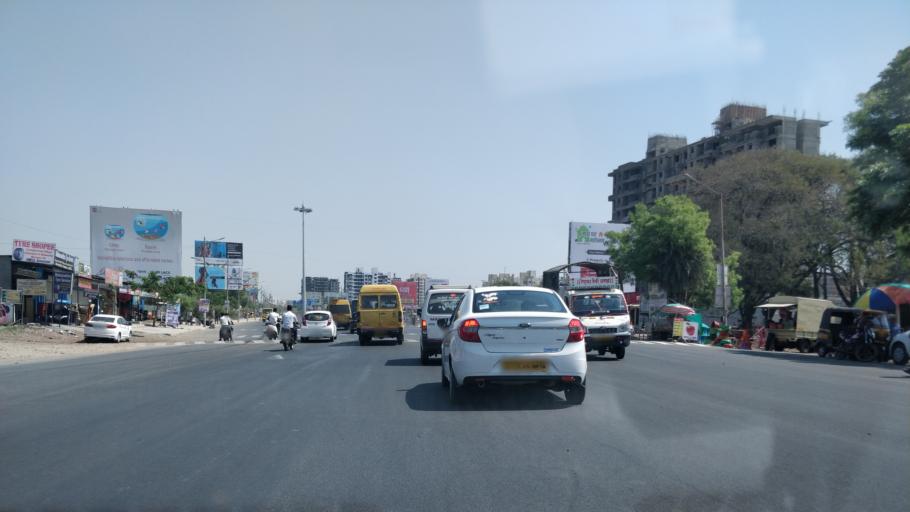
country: IN
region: Maharashtra
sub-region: Pune Division
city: Alandi
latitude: 18.6568
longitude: 73.8853
